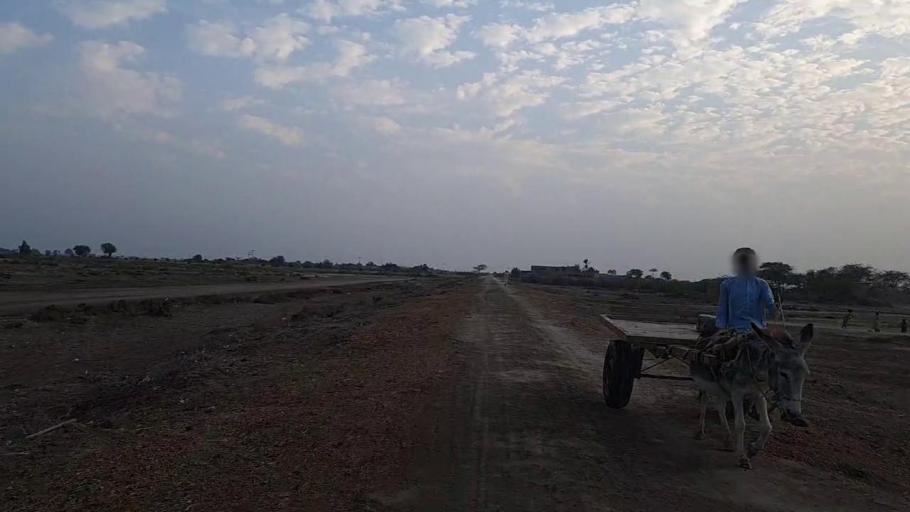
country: PK
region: Sindh
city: Pithoro
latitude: 25.4602
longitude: 69.3458
